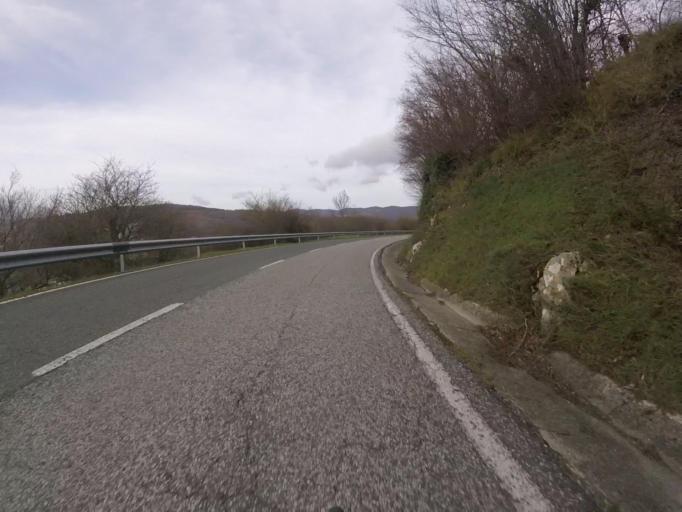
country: ES
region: Navarre
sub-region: Provincia de Navarra
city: Olazagutia
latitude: 42.8679
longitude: -2.1867
